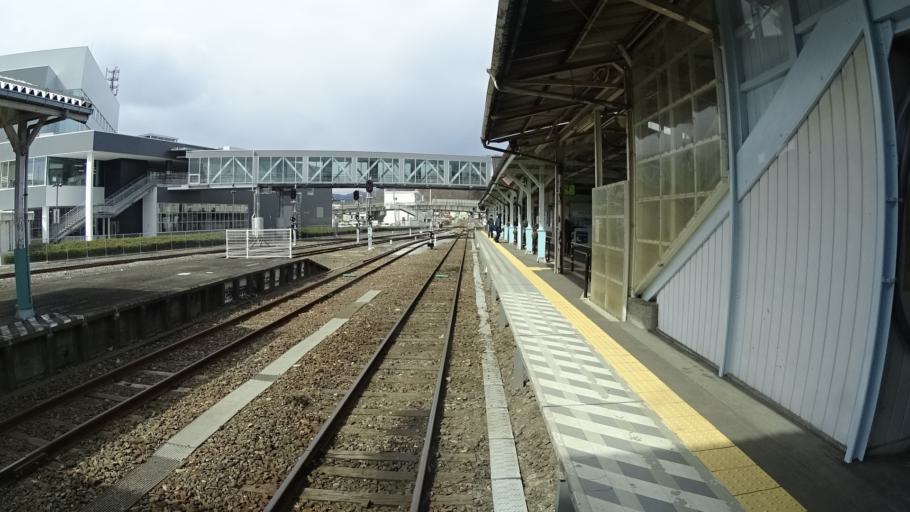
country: JP
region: Iwate
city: Miyako
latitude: 39.6401
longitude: 141.9469
